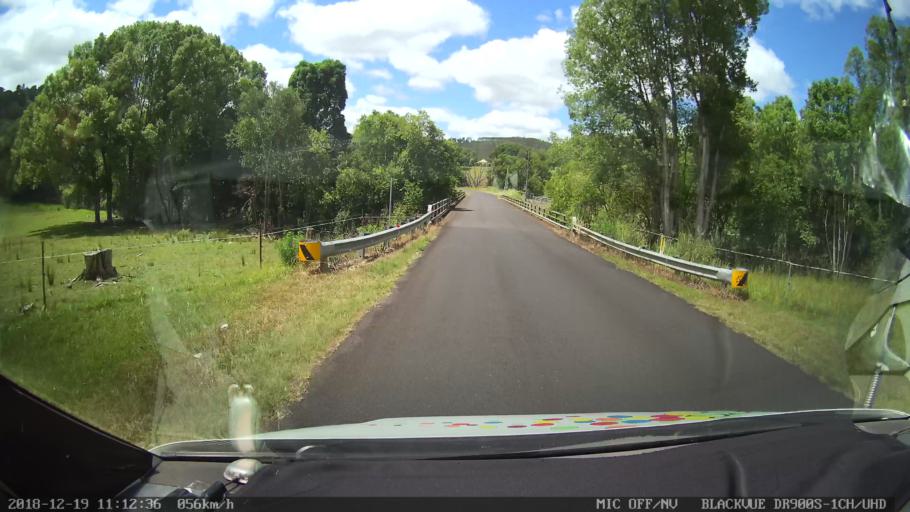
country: AU
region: New South Wales
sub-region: Lismore Municipality
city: Nimbin
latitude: -28.6502
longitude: 153.2602
